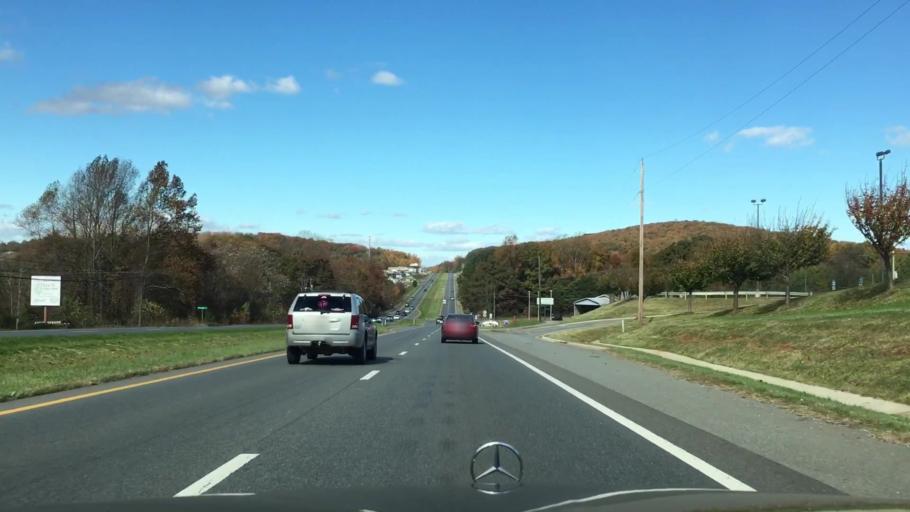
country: US
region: Virginia
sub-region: Campbell County
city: Rustburg
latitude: 37.2868
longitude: -79.1669
